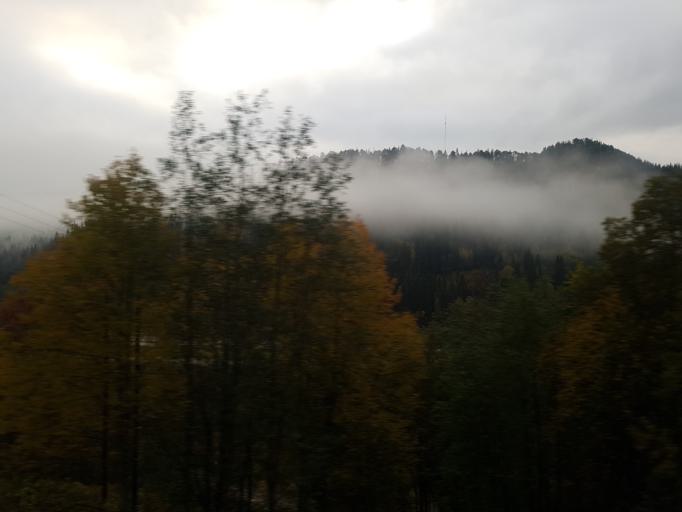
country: NO
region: Sor-Trondelag
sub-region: Midtre Gauldal
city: Storen
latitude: 63.0296
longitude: 10.2649
